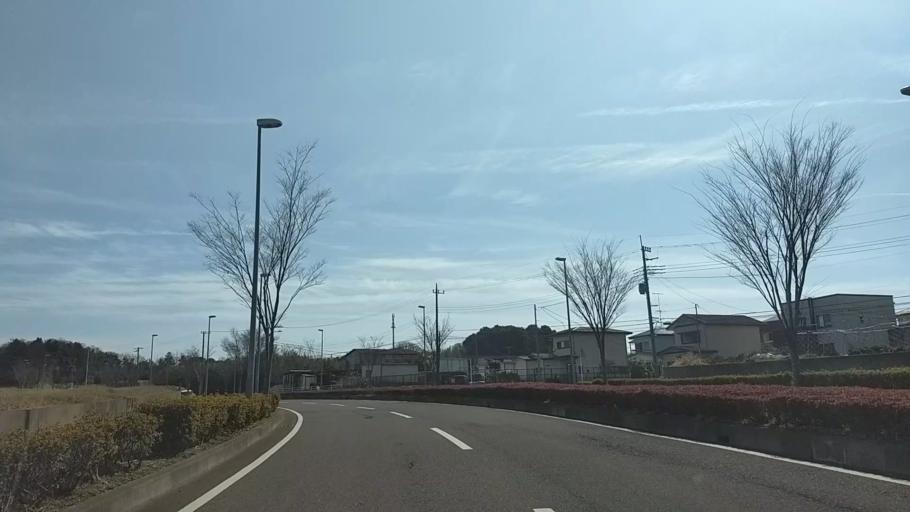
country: JP
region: Kanagawa
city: Fujisawa
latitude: 35.3825
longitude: 139.4311
